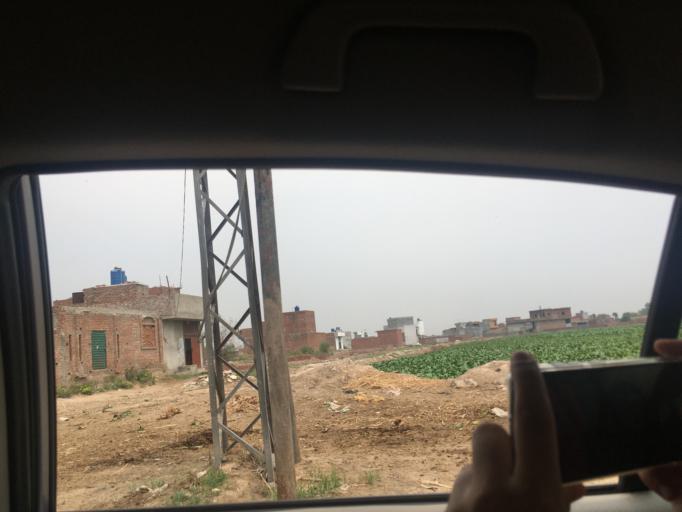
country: PK
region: Punjab
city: Lahore
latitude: 31.6212
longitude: 74.3468
